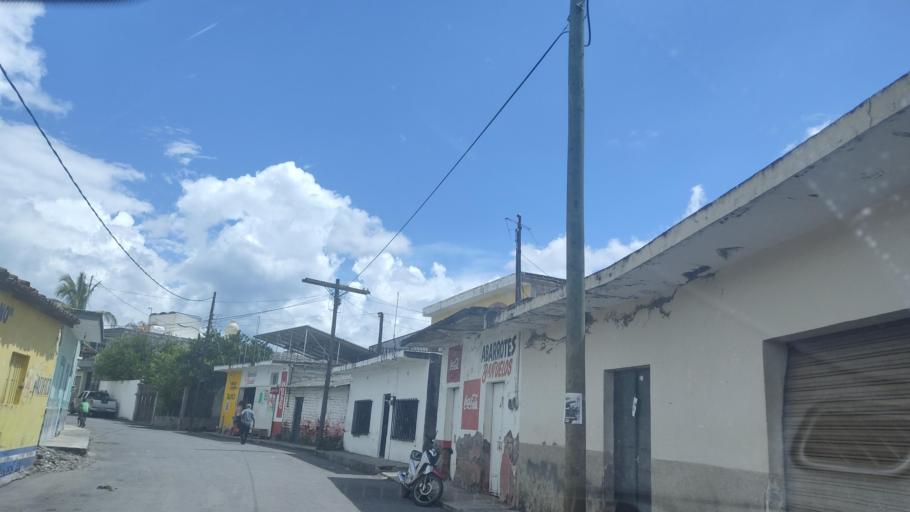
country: MX
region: Nayarit
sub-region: Ahuacatlan
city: Ahuacatlan
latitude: 21.1201
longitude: -104.6225
